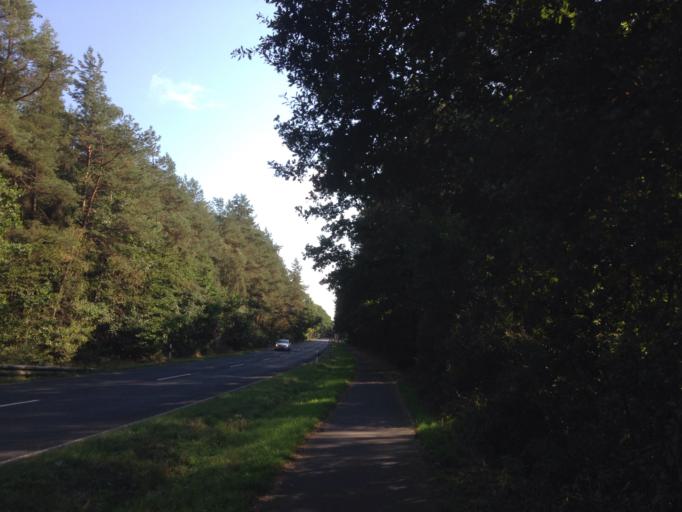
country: DE
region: Hesse
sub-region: Regierungsbezirk Giessen
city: Giessen
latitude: 50.5583
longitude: 8.6955
